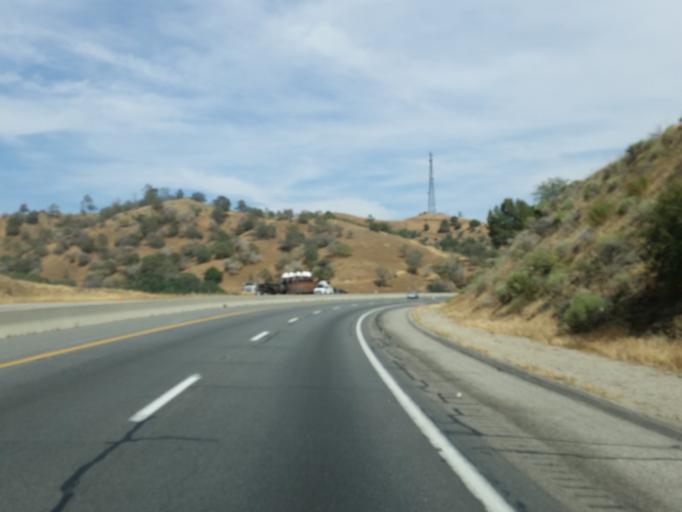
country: US
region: California
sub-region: Kern County
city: Bear Valley Springs
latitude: 35.2560
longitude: -118.6103
